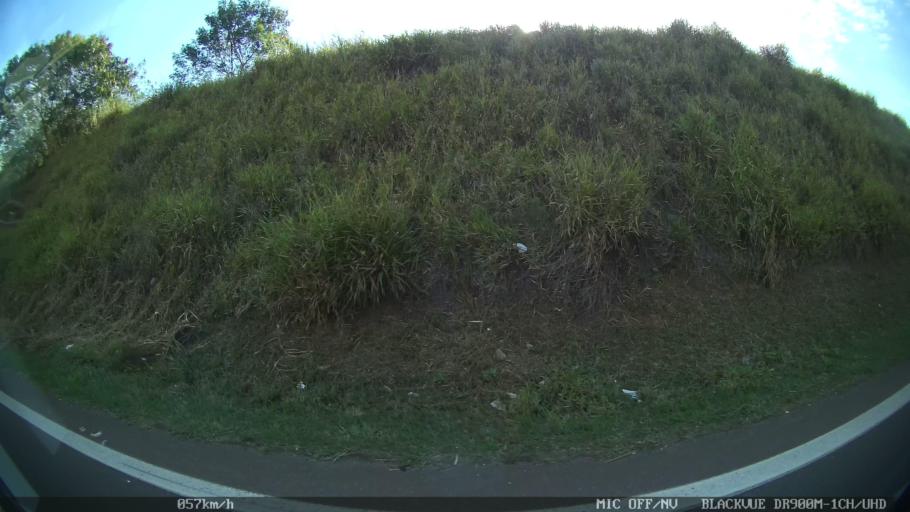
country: BR
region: Sao Paulo
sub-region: Piracicaba
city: Piracicaba
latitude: -22.6934
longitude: -47.6021
